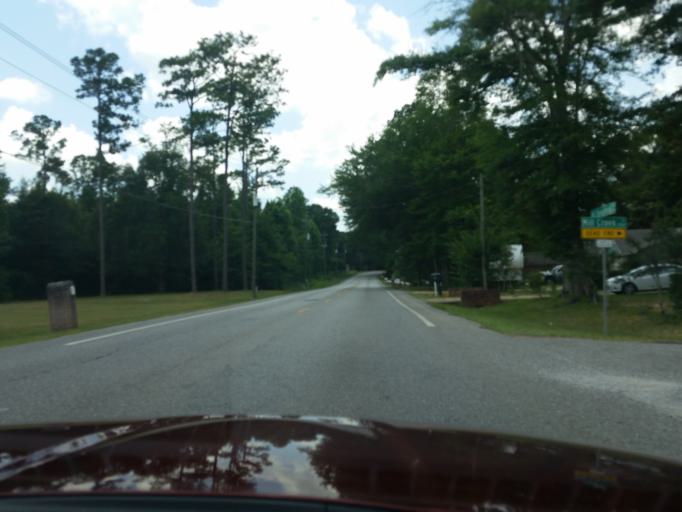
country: US
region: Florida
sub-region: Escambia County
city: Gonzalez
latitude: 30.5829
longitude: -87.2729
